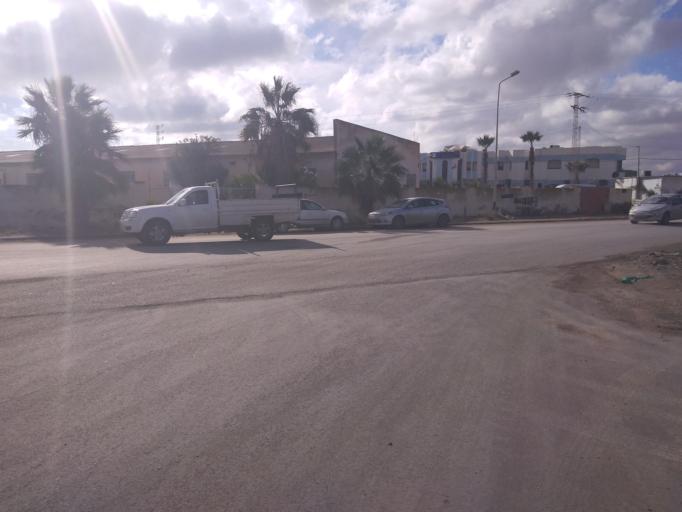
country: TN
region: Safaqis
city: Sfax
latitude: 34.7261
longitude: 10.7612
